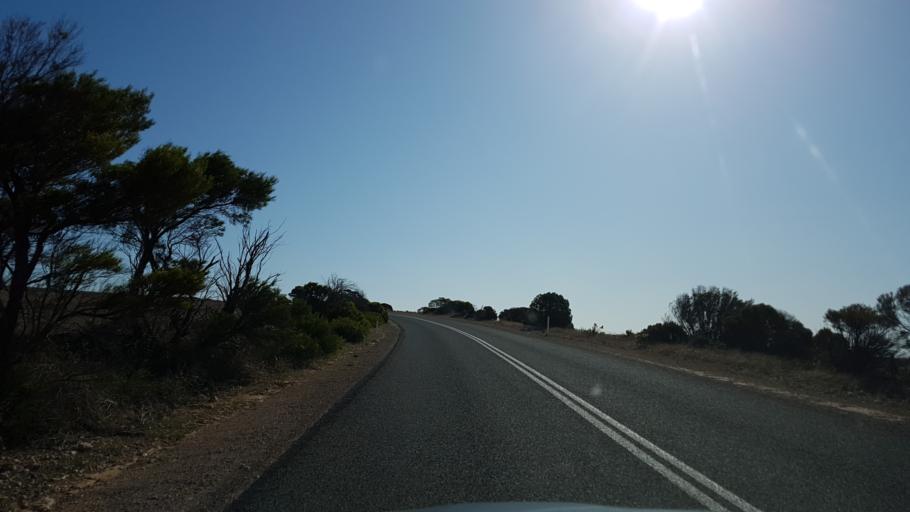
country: AU
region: South Australia
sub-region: Mid Murray
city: Mannum
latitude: -34.7749
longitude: 139.5425
